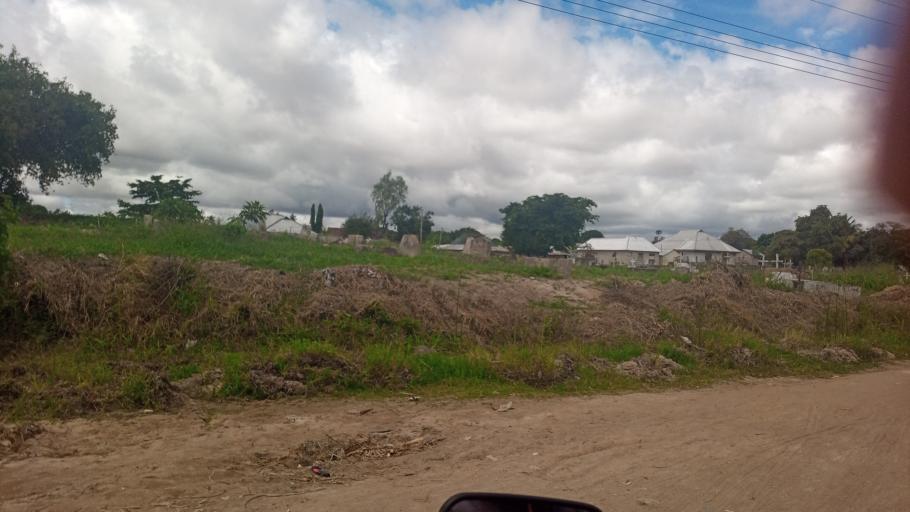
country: TZ
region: Dodoma
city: Dodoma
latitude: -6.1884
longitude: 35.7251
